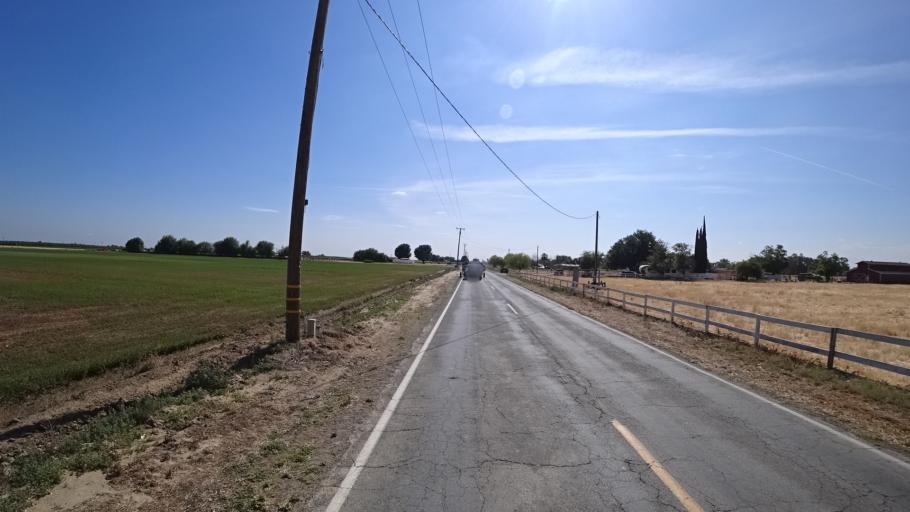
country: US
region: California
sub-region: Kings County
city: Lemoore
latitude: 36.2547
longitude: -119.7581
